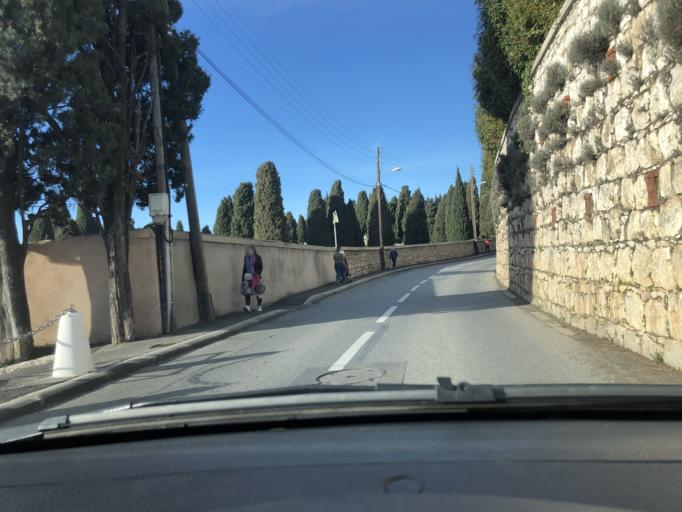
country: FR
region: Provence-Alpes-Cote d'Azur
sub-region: Departement des Alpes-Maritimes
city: Saint-Laurent-du-Var
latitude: 43.6775
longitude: 7.2166
